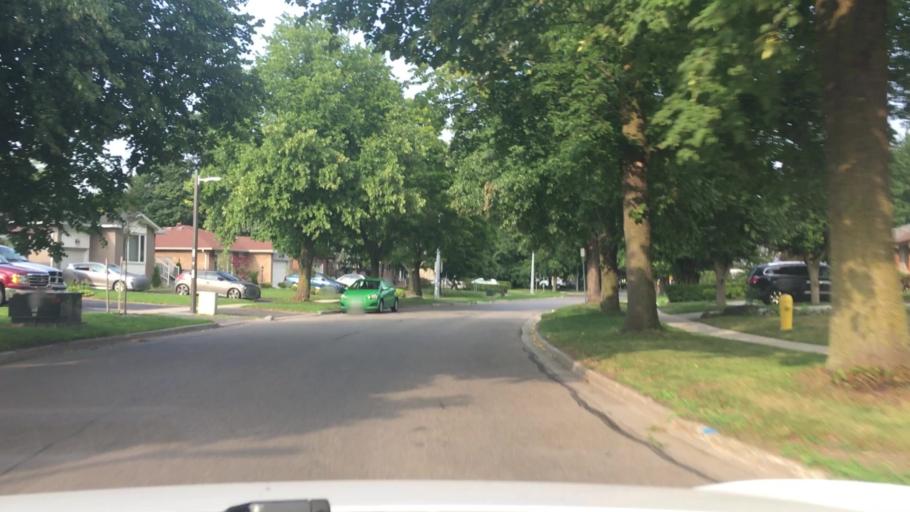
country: CA
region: Ontario
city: Ajax
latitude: 43.8732
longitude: -78.9592
